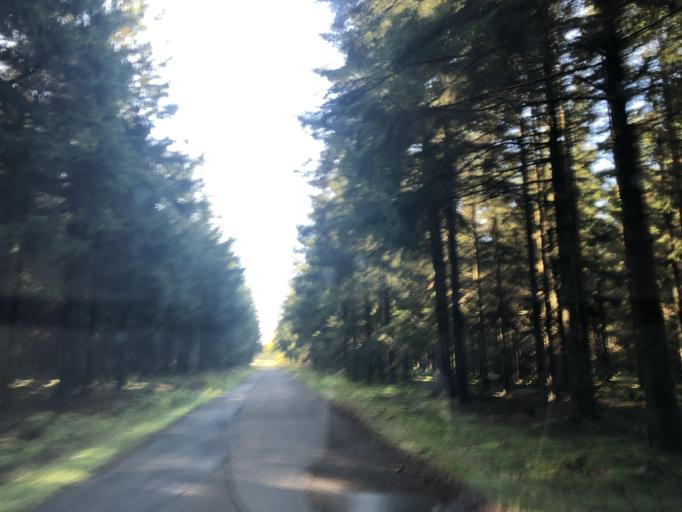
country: DK
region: Central Jutland
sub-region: Holstebro Kommune
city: Holstebro
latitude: 56.3141
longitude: 8.5052
